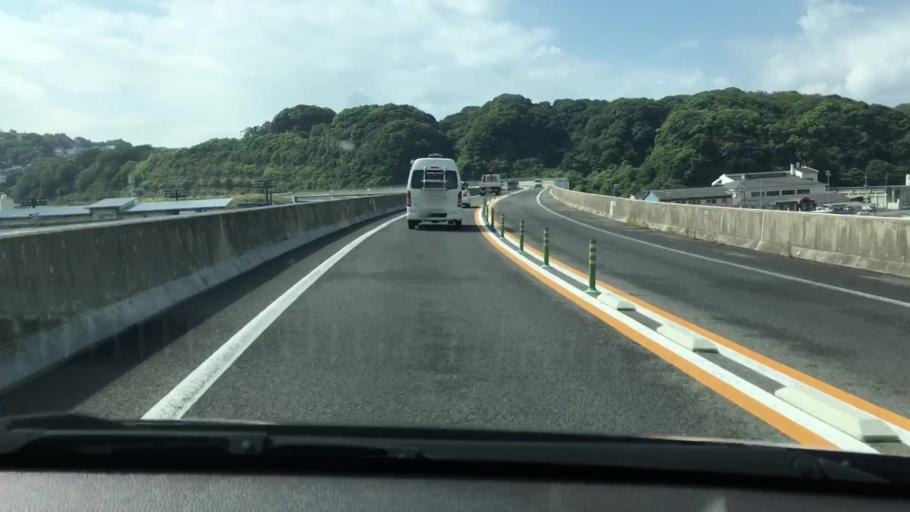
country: JP
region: Nagasaki
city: Sasebo
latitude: 33.1575
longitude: 129.7295
